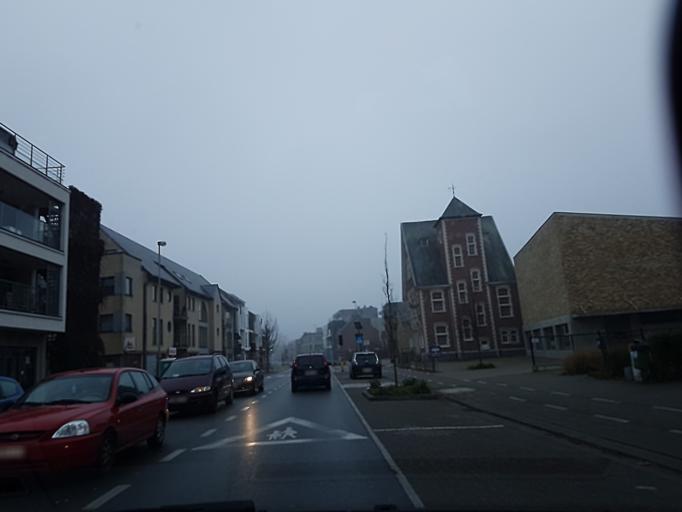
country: BE
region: Flanders
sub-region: Provincie Antwerpen
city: Bonheiden
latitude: 51.0221
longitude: 4.5484
